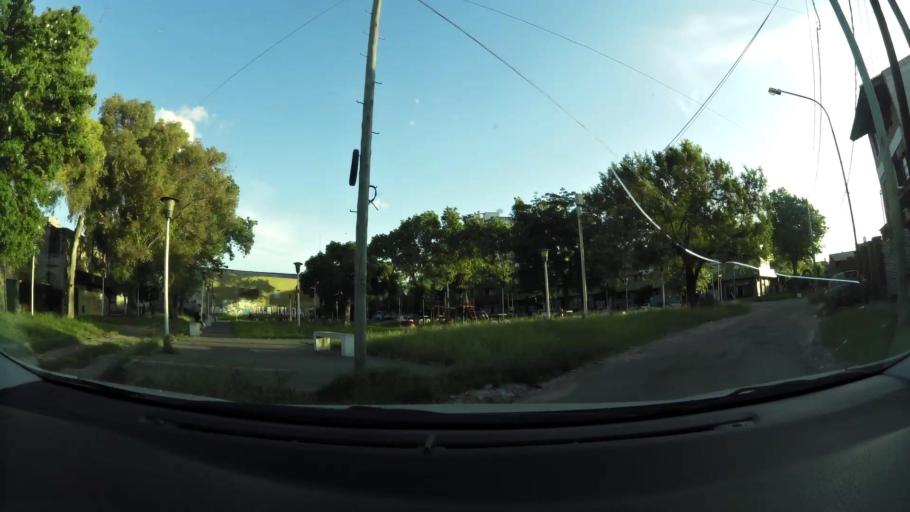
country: AR
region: Buenos Aires F.D.
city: Villa Lugano
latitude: -34.6952
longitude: -58.4796
